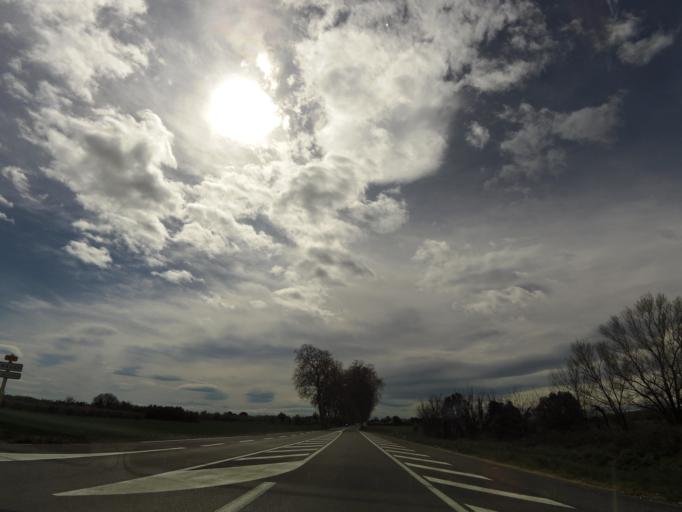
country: FR
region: Languedoc-Roussillon
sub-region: Departement du Gard
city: Codognan
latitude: 43.7236
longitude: 4.2130
